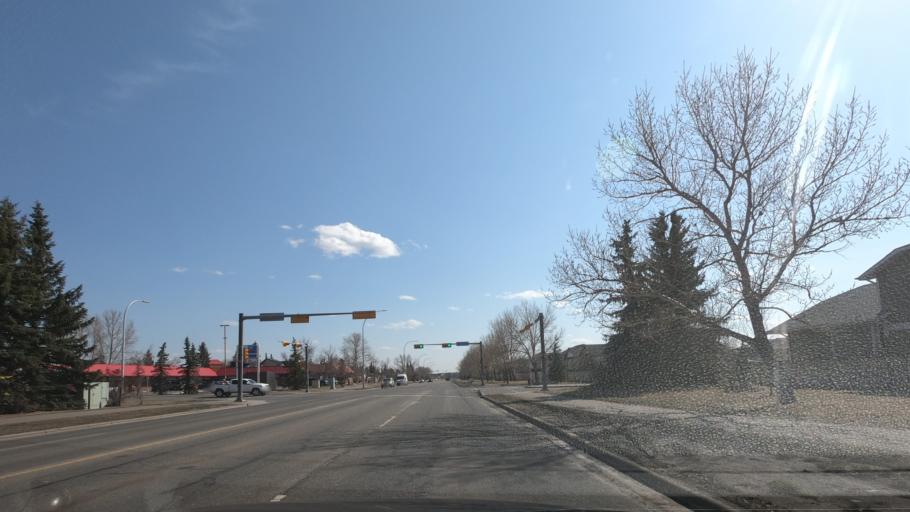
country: CA
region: Alberta
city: Airdrie
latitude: 51.2763
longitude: -113.9899
